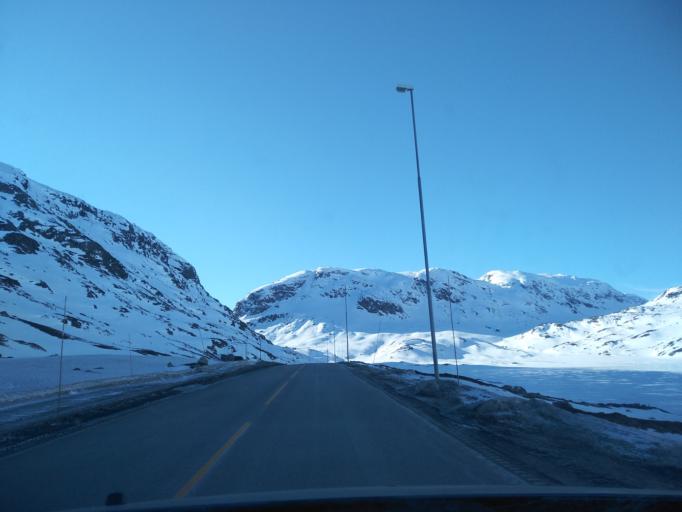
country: NO
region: Aust-Agder
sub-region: Bykle
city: Hovden
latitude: 59.8504
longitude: 7.0933
